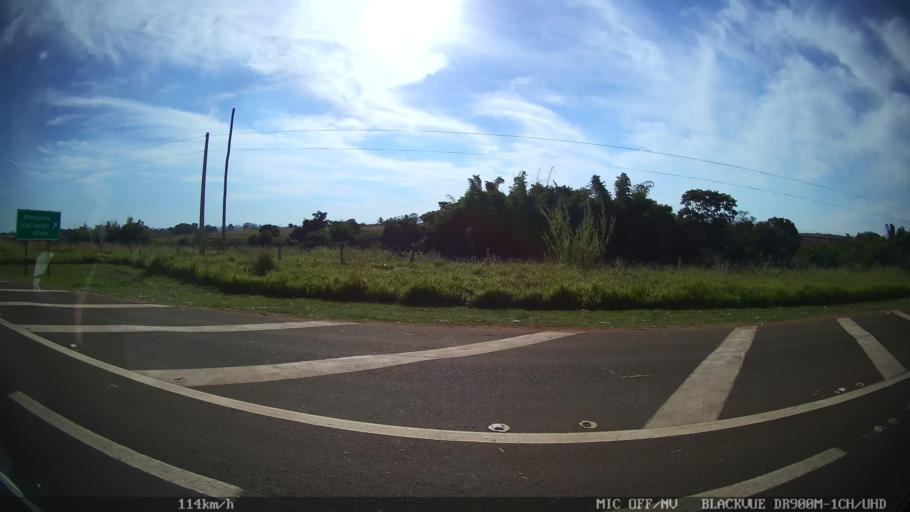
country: BR
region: Sao Paulo
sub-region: Araraquara
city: Araraquara
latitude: -21.7912
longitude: -48.1287
